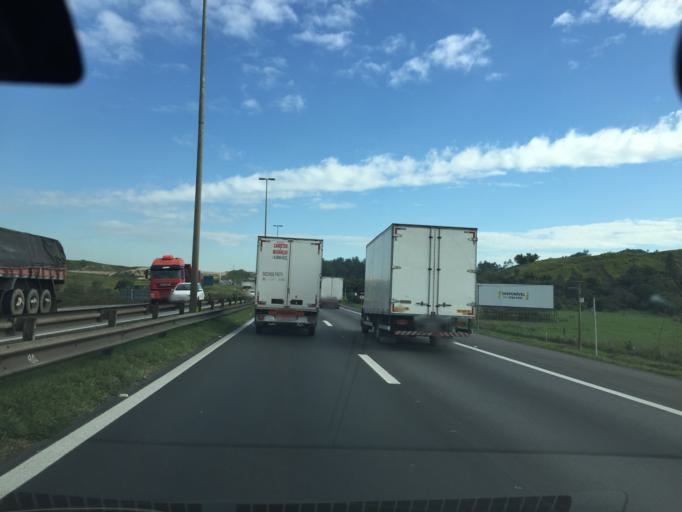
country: BR
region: Sao Paulo
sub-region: Jacarei
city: Jacarei
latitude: -23.2922
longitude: -46.0010
